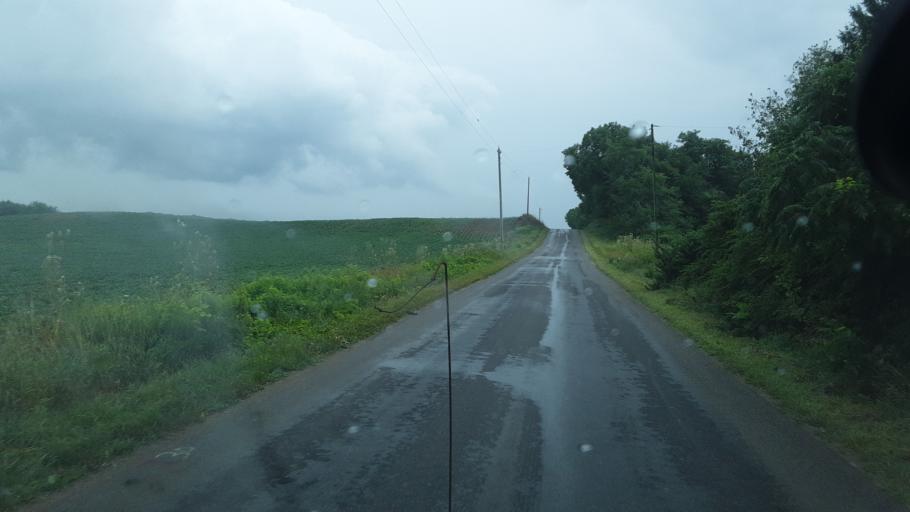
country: US
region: Indiana
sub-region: Steuben County
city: Hamilton
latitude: 41.5557
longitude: -84.8553
